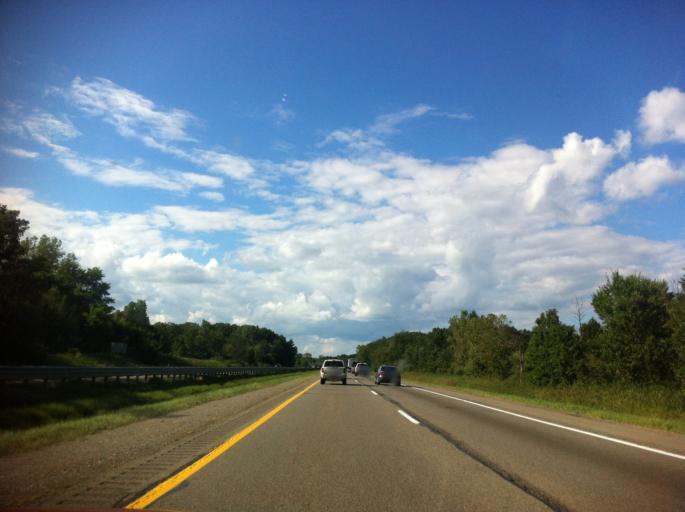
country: US
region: Michigan
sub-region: Livingston County
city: Whitmore Lake
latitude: 42.3592
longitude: -83.7486
